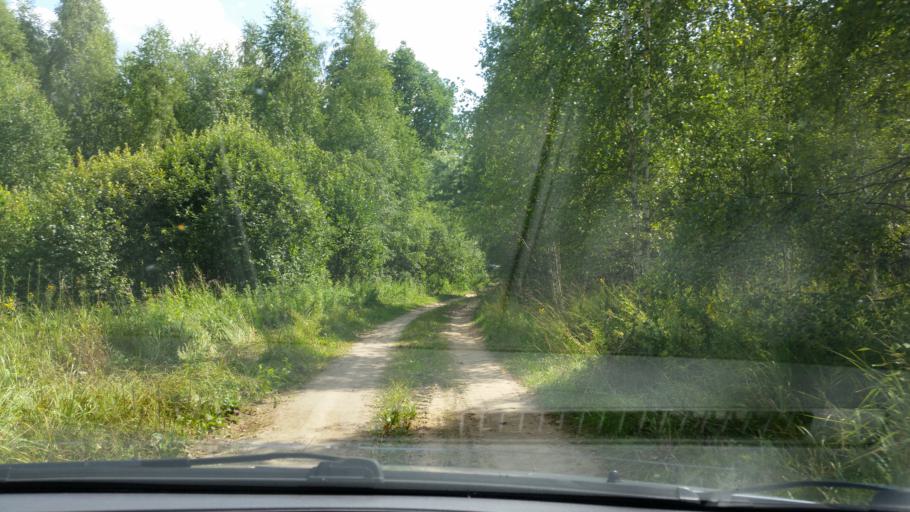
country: RU
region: Moskovskaya
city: Pushchino
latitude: 54.9285
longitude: 37.7063
